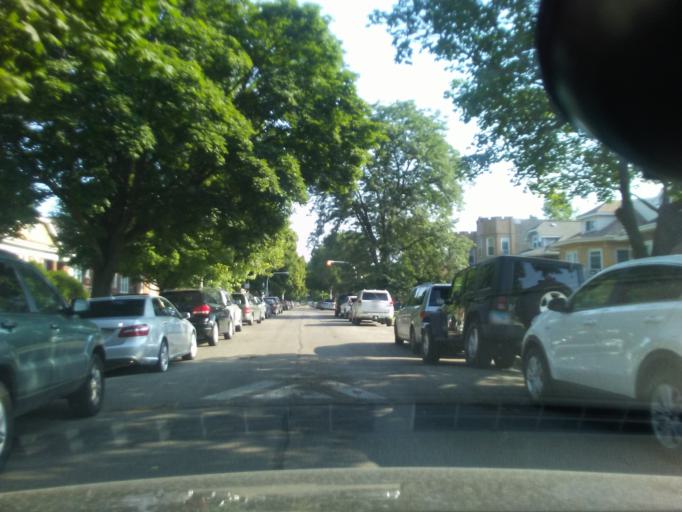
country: US
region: Illinois
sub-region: Cook County
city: Elmwood Park
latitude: 41.9342
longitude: -87.7639
